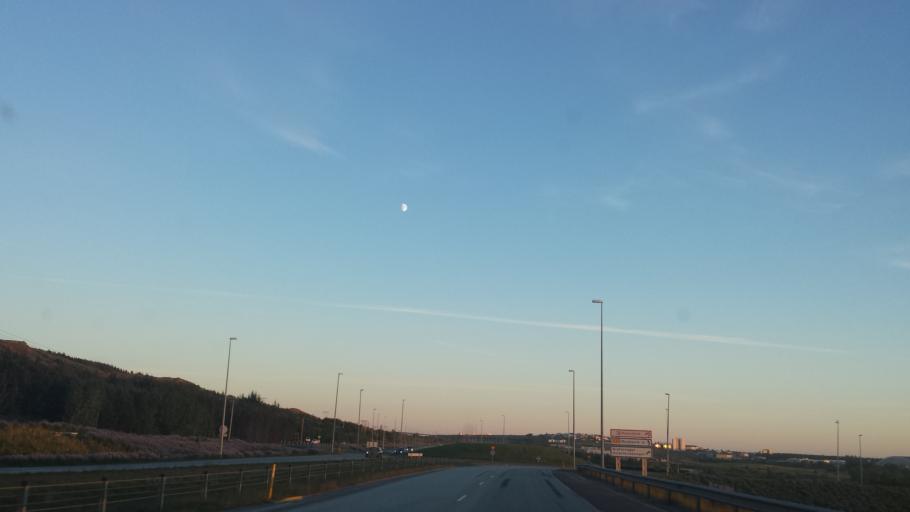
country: IS
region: Capital Region
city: Mosfellsbaer
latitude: 64.1547
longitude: -21.7355
